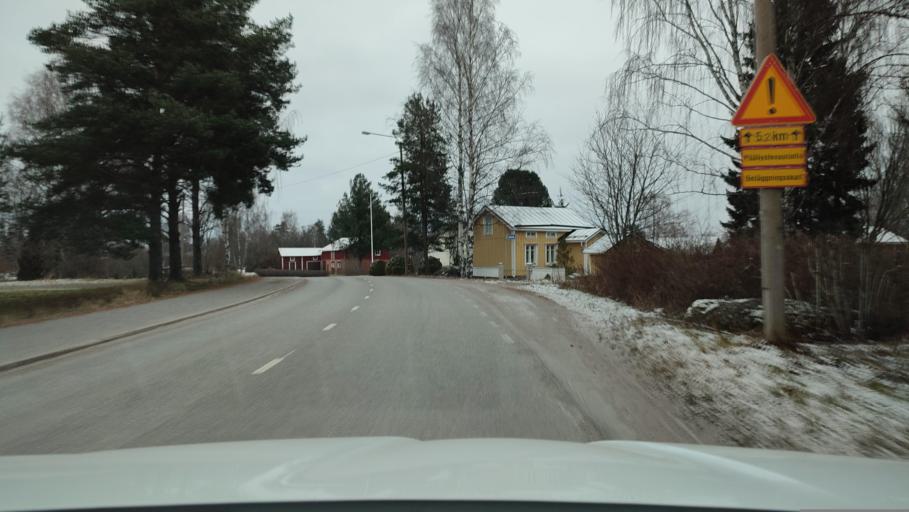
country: FI
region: Ostrobothnia
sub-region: Vaasa
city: Smedsby
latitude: 63.1549
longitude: 21.6930
